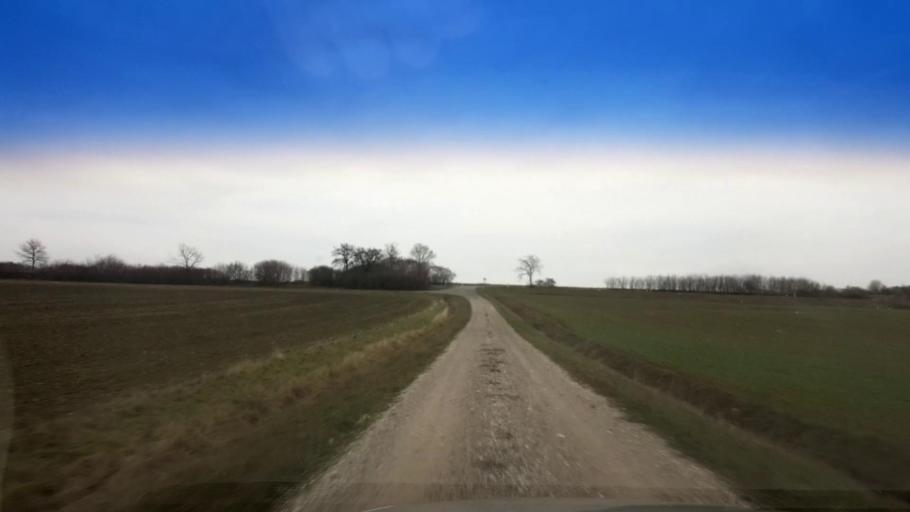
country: DE
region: Bavaria
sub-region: Upper Franconia
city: Hallerndorf
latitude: 49.7709
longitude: 10.9364
